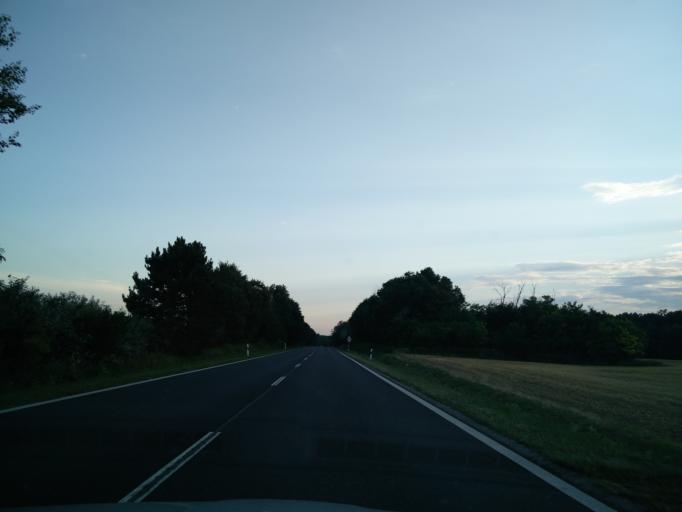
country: HU
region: Vas
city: Janoshaza
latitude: 47.1068
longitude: 17.0936
